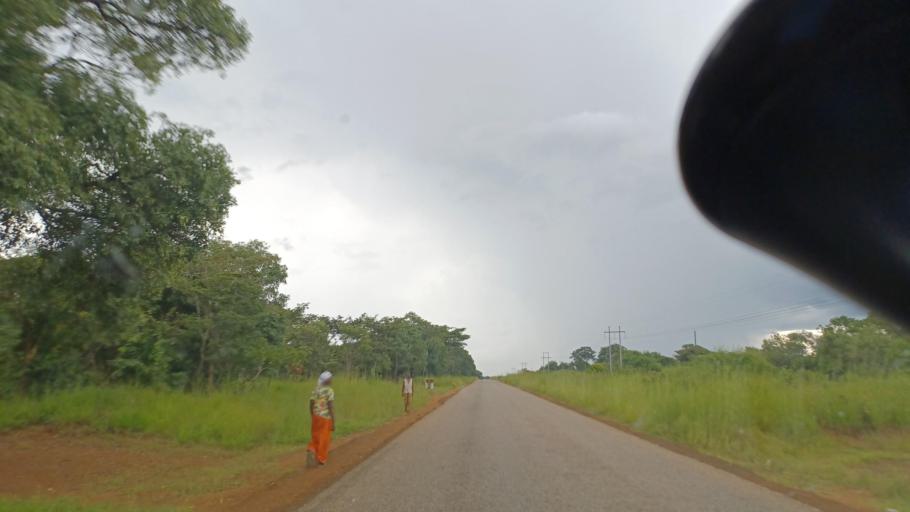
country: ZM
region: North-Western
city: Kasempa
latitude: -13.0242
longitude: 25.9993
